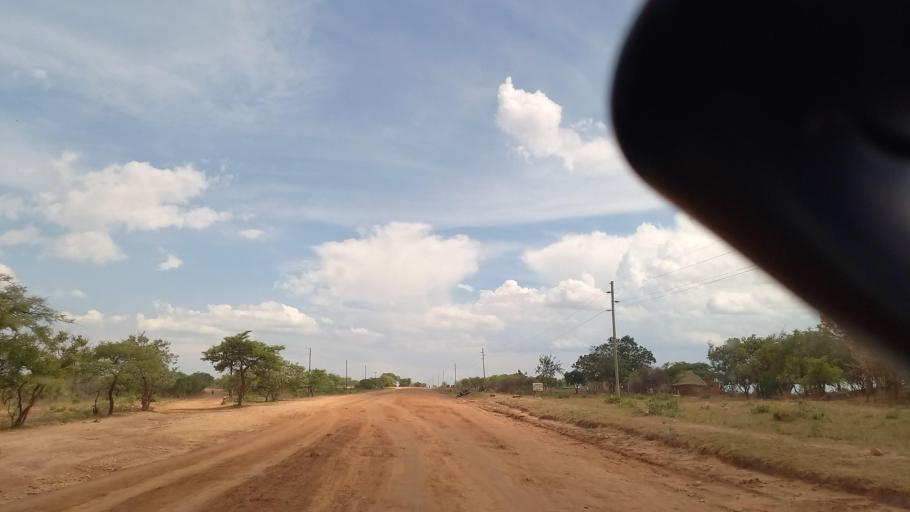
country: ZM
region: Lusaka
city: Kafue
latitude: -16.1430
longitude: 28.0543
